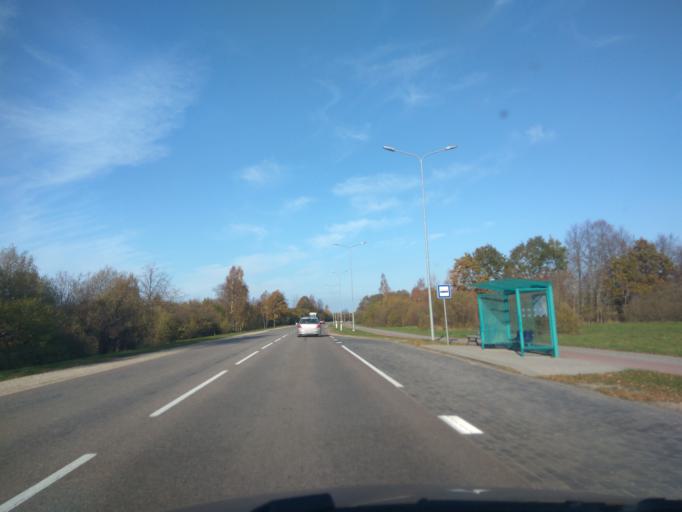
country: LV
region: Ventspils
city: Ventspils
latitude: 57.3604
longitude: 21.5632
